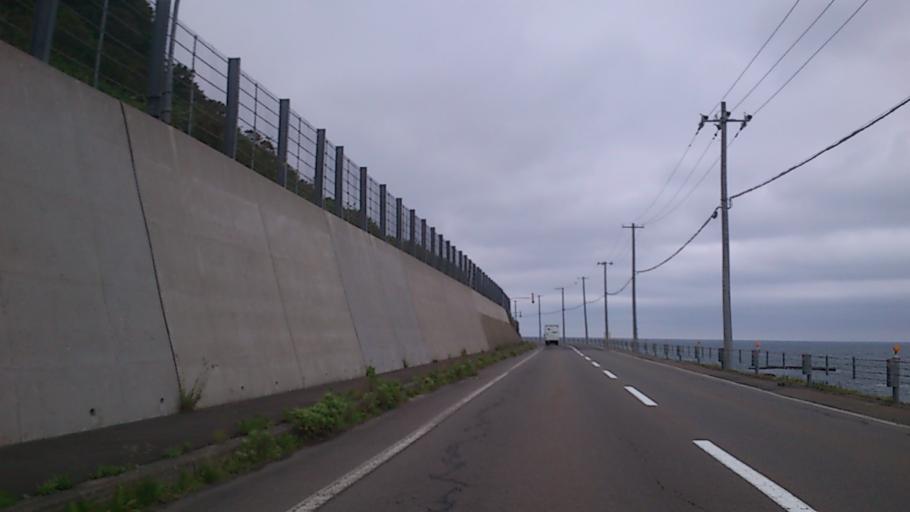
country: JP
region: Hokkaido
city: Iwanai
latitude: 42.6881
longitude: 139.9287
